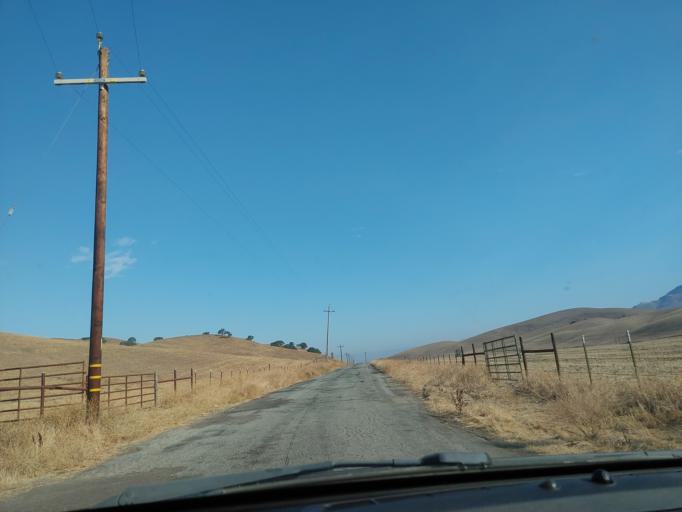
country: US
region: California
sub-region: San Benito County
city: Ridgemark
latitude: 36.7981
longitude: -121.2695
